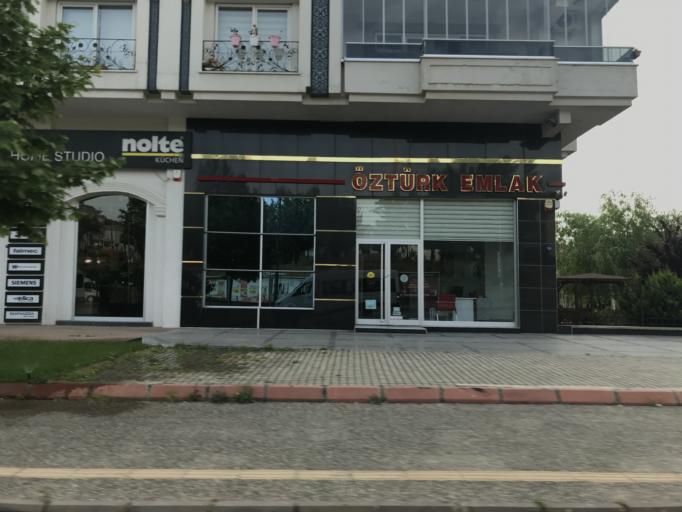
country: TR
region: Gaziantep
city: Sahinbey
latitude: 37.0579
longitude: 37.3318
